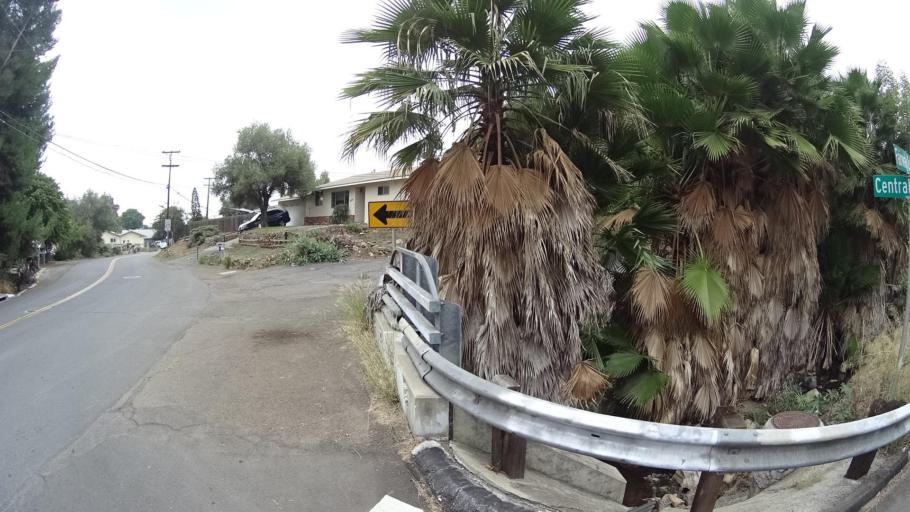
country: US
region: California
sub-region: San Diego County
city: Spring Valley
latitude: 32.7413
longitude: -117.0096
